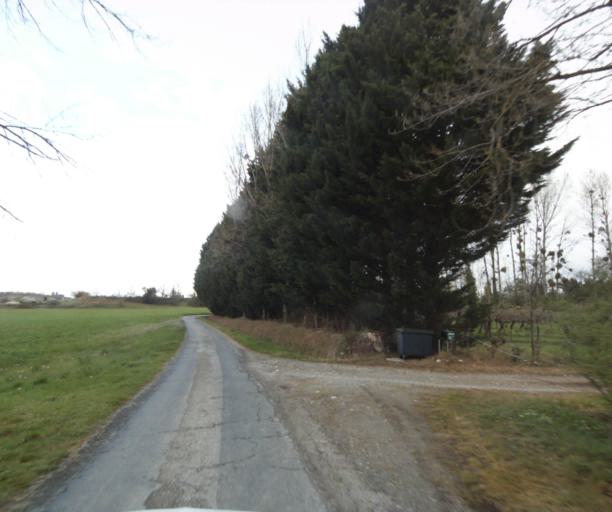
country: FR
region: Midi-Pyrenees
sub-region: Departement de l'Ariege
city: Saverdun
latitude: 43.2261
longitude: 1.5959
